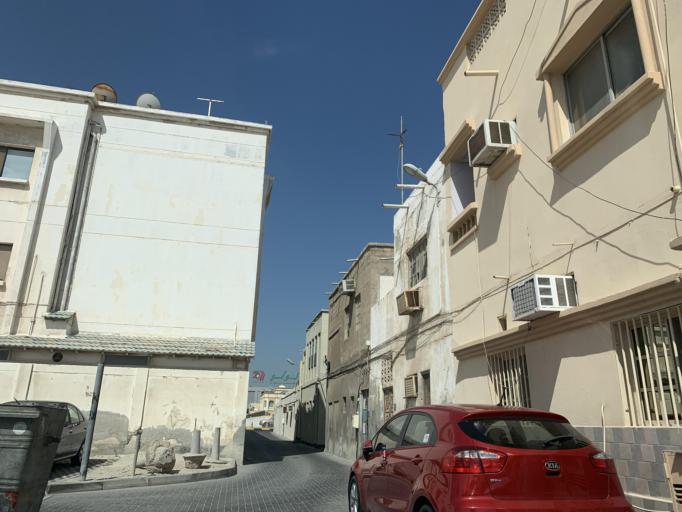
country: BH
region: Muharraq
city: Al Muharraq
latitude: 26.2557
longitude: 50.6087
